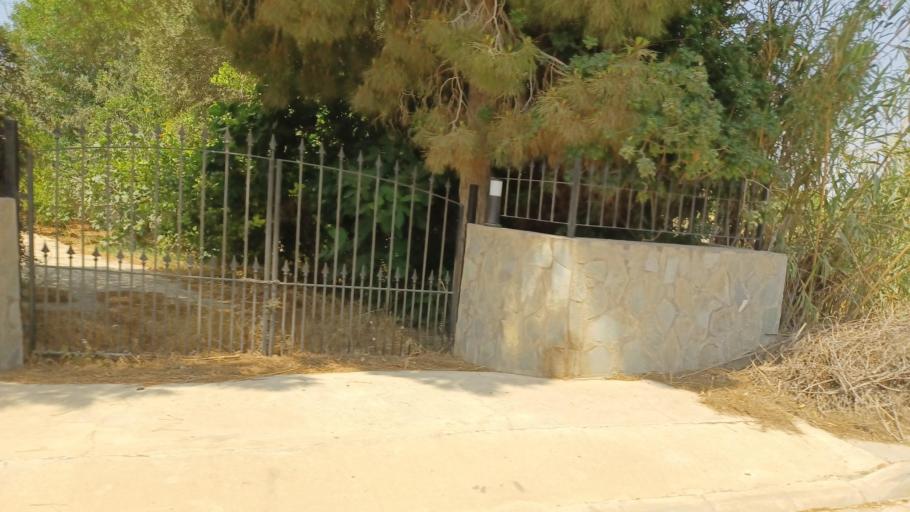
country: CY
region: Ammochostos
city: Ayia Napa
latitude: 34.9812
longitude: 34.0234
